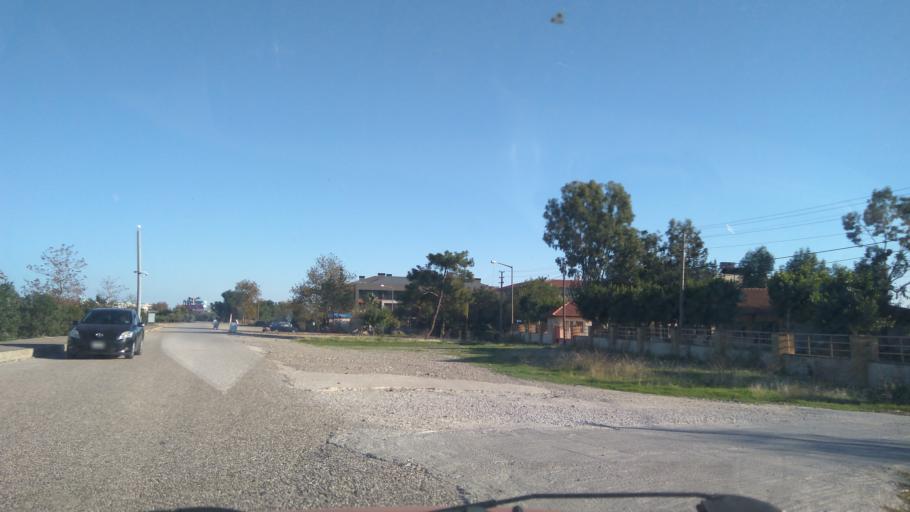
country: TR
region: Antalya
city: Kemer
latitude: 36.5667
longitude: 30.5655
